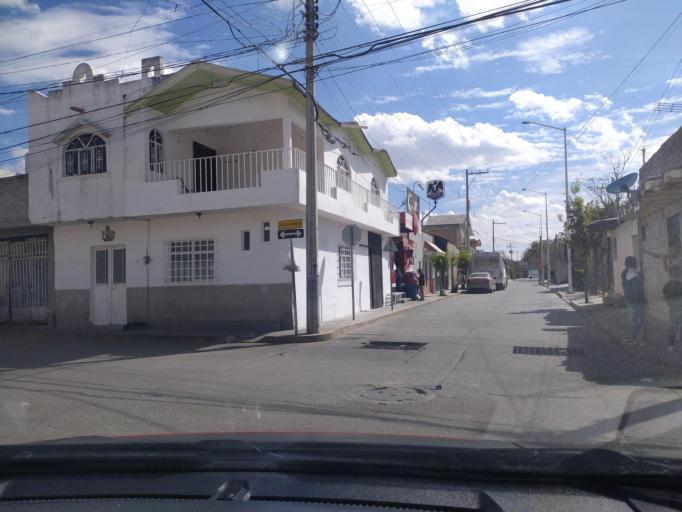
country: MX
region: Guanajuato
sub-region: San Francisco del Rincon
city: Fraccionamiento la Mezquitera
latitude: 21.0230
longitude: -101.8304
